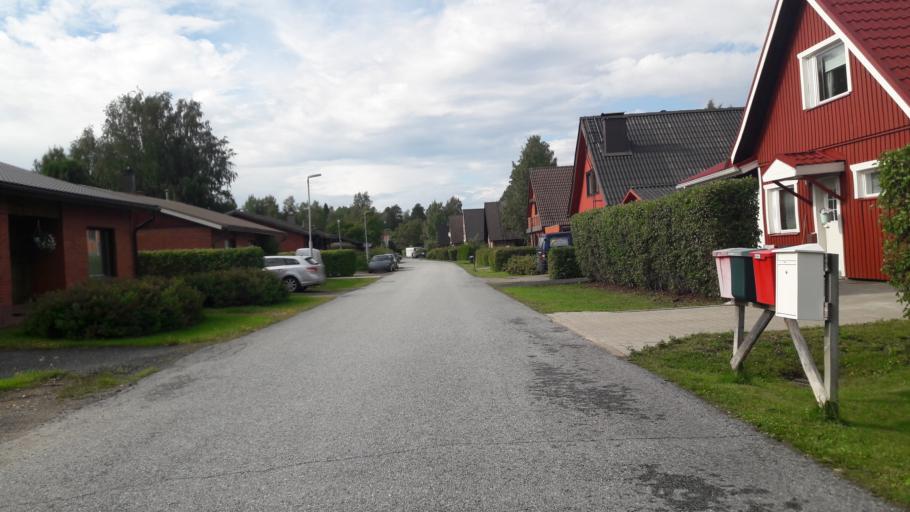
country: FI
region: North Karelia
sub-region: Joensuu
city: Joensuu
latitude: 62.5798
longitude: 29.8110
